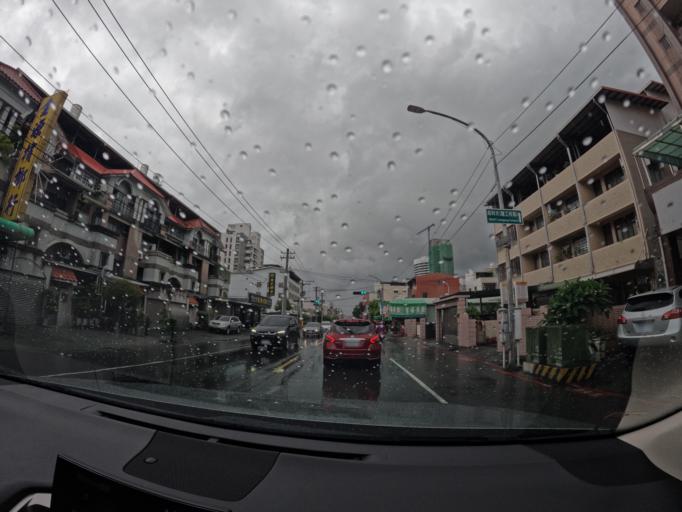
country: TW
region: Taiwan
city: Fengshan
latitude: 22.6482
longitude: 120.3461
